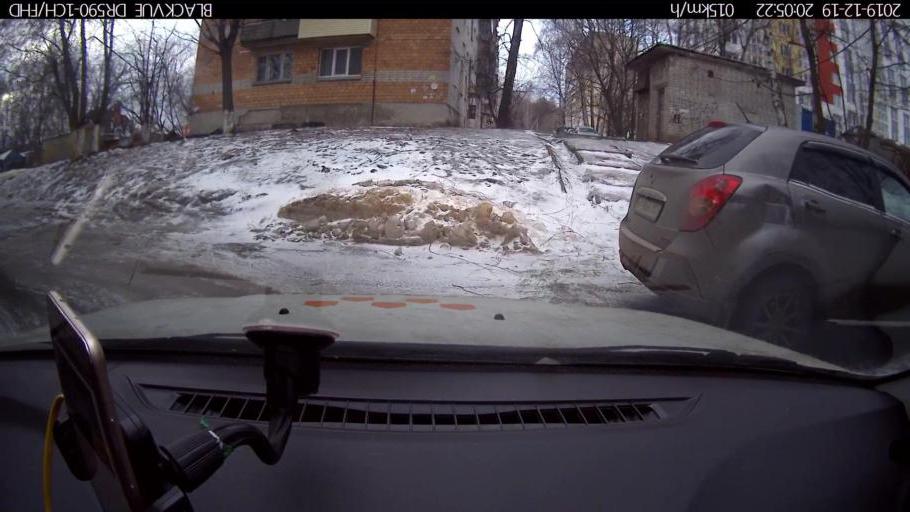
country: RU
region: Nizjnij Novgorod
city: Nizhniy Novgorod
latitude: 56.2995
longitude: 44.0058
